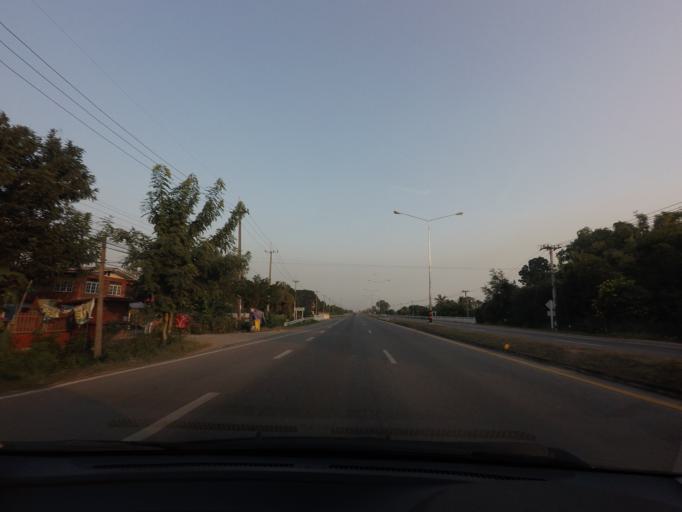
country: TH
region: Sukhothai
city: Sukhothai
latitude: 17.0213
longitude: 99.8984
